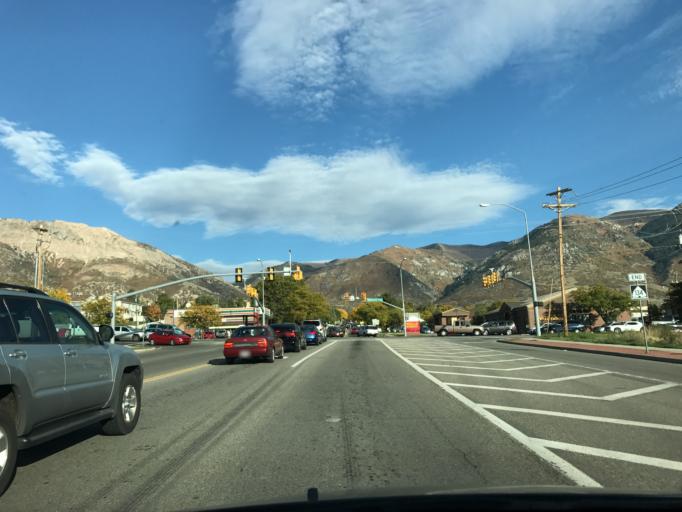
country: US
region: Utah
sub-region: Weber County
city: North Ogden
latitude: 41.3059
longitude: -111.9696
